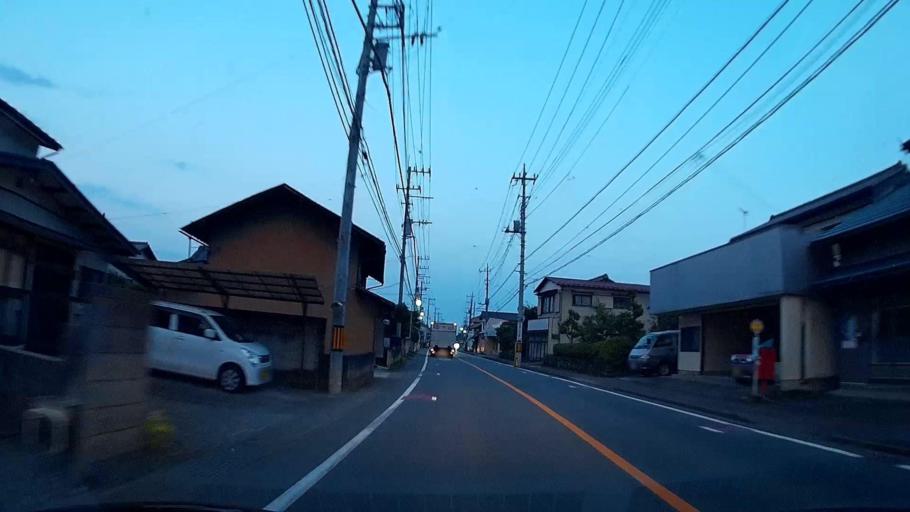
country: JP
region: Gunma
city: Annaka
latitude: 36.3783
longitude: 138.8879
